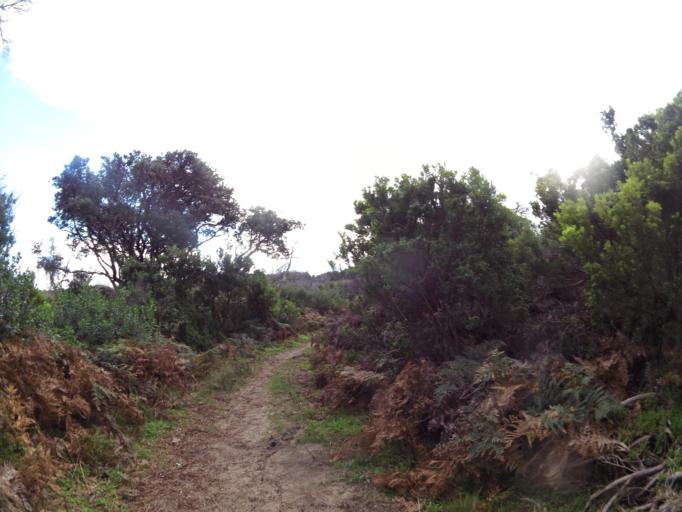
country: AU
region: Victoria
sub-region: Bass Coast
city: North Wonthaggi
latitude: -38.6363
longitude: 145.5543
